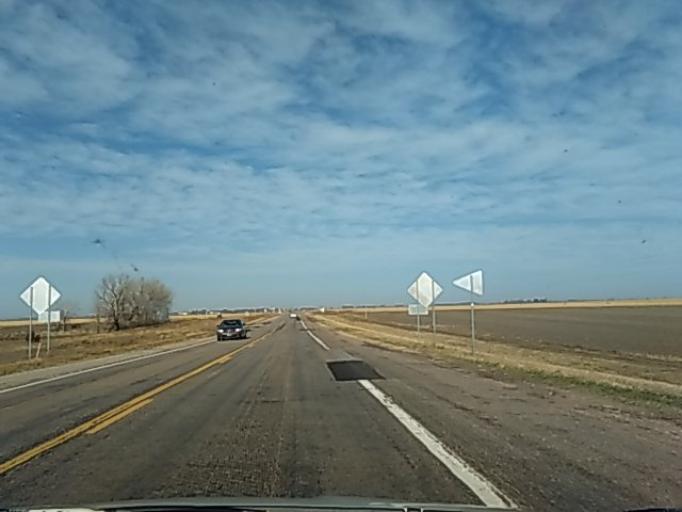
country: US
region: Nebraska
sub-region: Clay County
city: Clay Center
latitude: 40.4061
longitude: -98.0516
